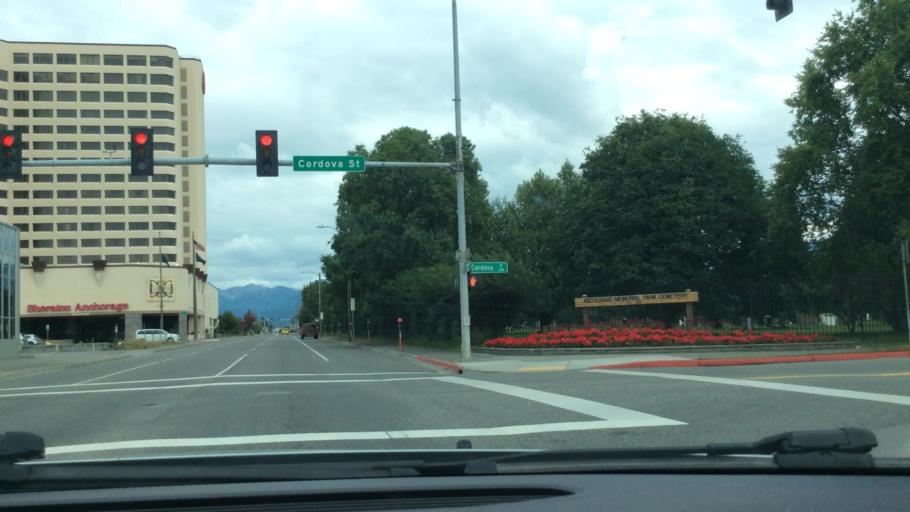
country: US
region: Alaska
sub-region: Anchorage Municipality
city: Anchorage
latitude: 61.2166
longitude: -149.8794
